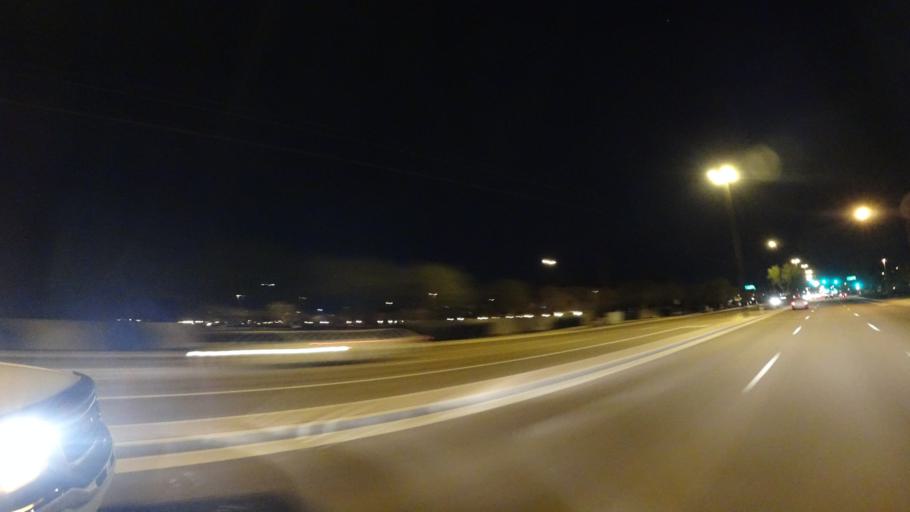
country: US
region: Arizona
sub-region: Maricopa County
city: Gilbert
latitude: 33.3009
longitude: -111.7557
